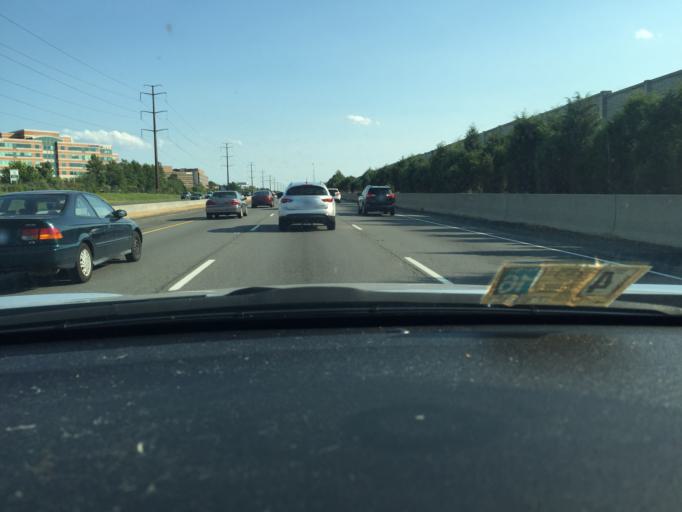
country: US
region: Virginia
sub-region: Fairfax County
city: Floris
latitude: 38.9394
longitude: -77.4299
